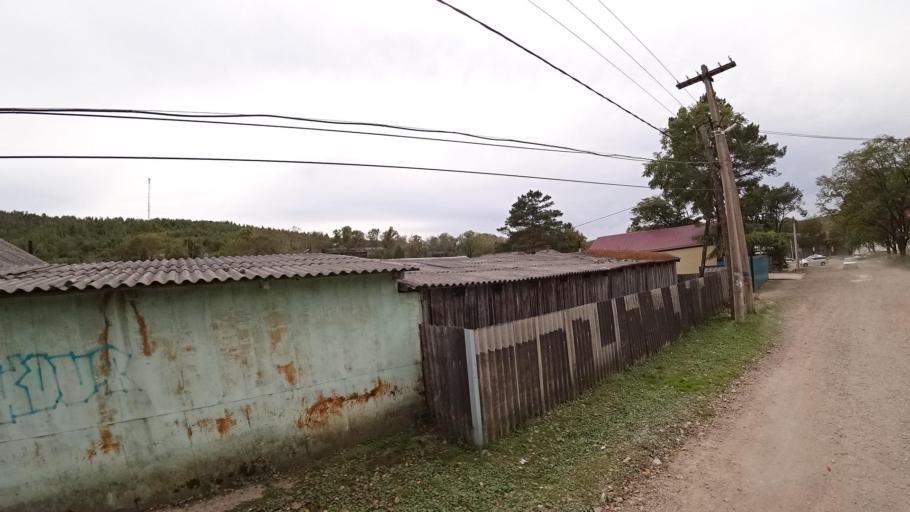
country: RU
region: Jewish Autonomous Oblast
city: Khingansk
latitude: 49.0207
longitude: 131.0635
